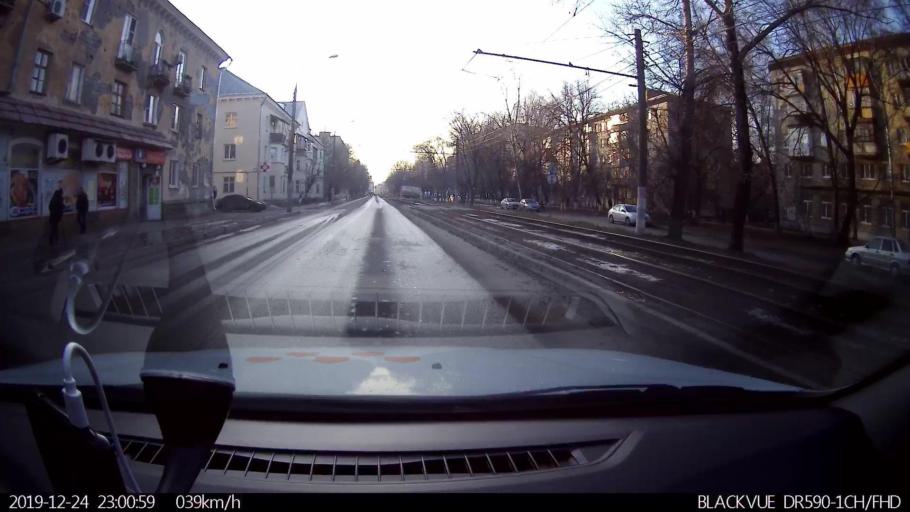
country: RU
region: Nizjnij Novgorod
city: Nizhniy Novgorod
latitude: 56.2707
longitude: 43.9305
